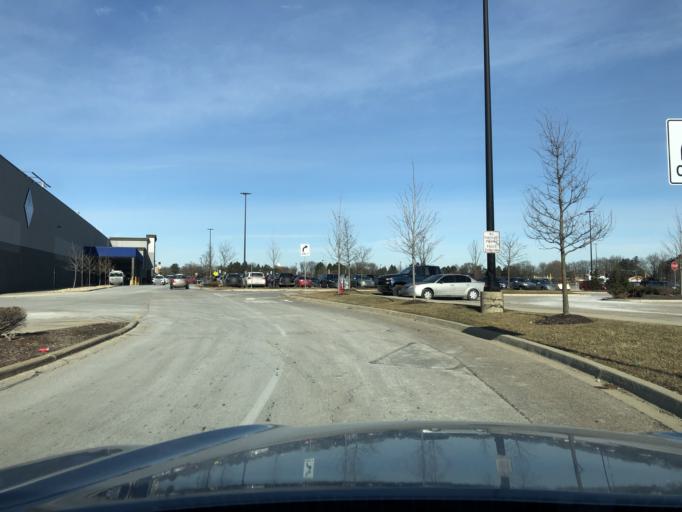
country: US
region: Illinois
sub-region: Lake County
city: Grandwood Park
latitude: 42.3859
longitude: -87.9658
